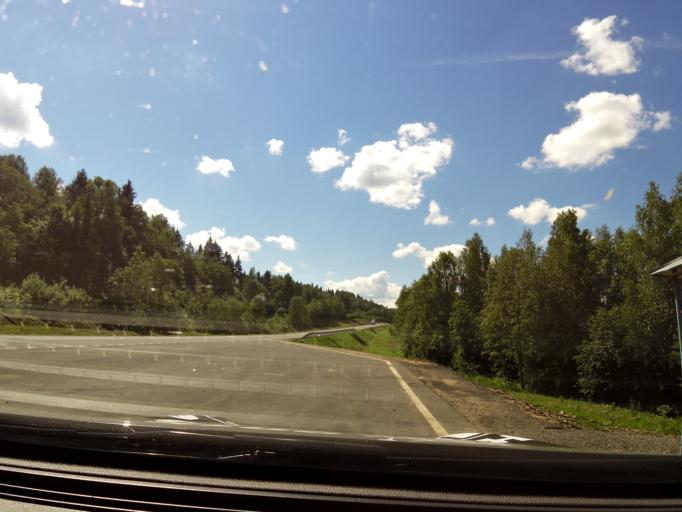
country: RU
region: Vologda
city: Ferapontovo
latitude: 60.0309
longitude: 38.5799
